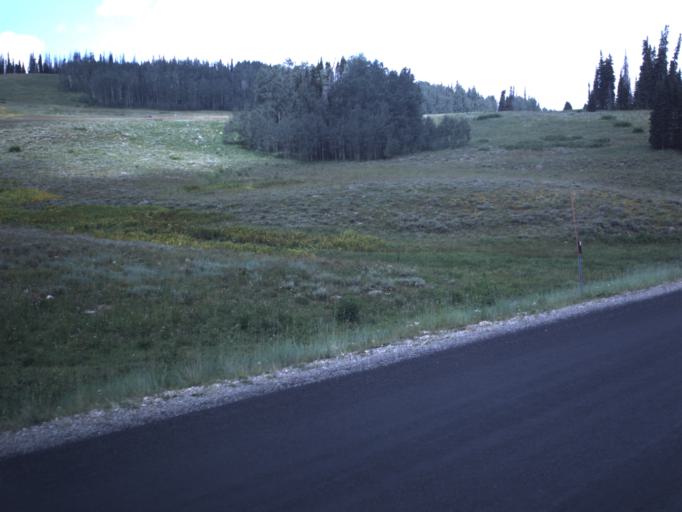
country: US
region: Utah
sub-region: Summit County
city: Francis
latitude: 40.4844
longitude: -111.0262
